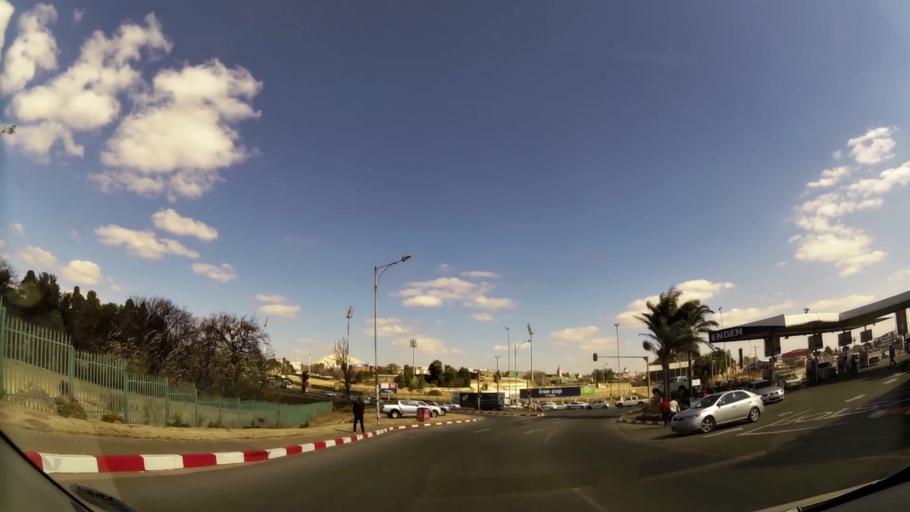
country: ZA
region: Gauteng
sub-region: West Rand District Municipality
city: Krugersdorp
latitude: -26.1000
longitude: 27.7807
